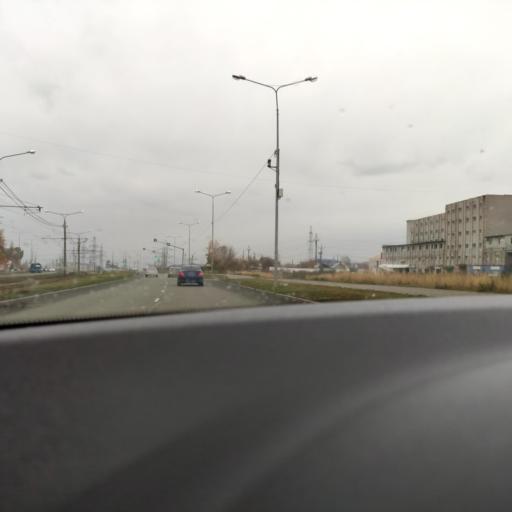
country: RU
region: Samara
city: Samara
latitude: 53.2666
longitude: 50.2307
